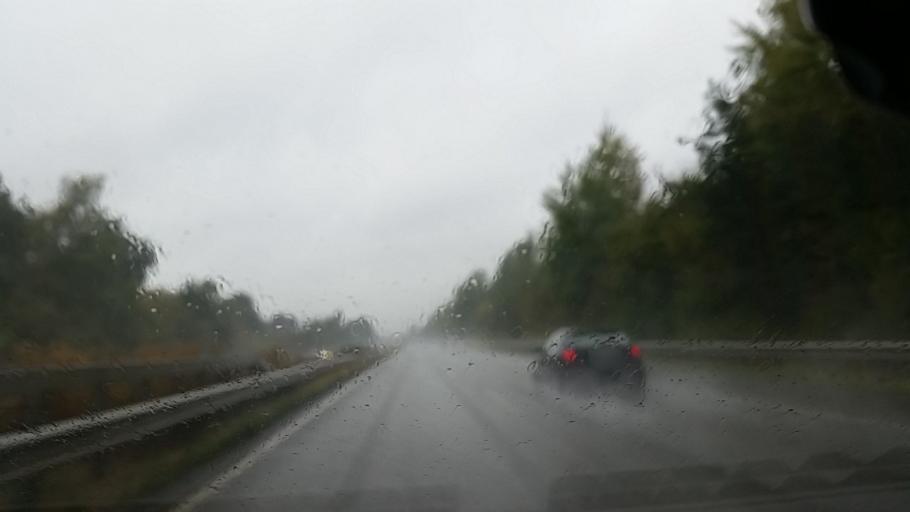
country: DE
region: Schleswig-Holstein
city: Bornsen
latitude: 53.4635
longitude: 10.2800
